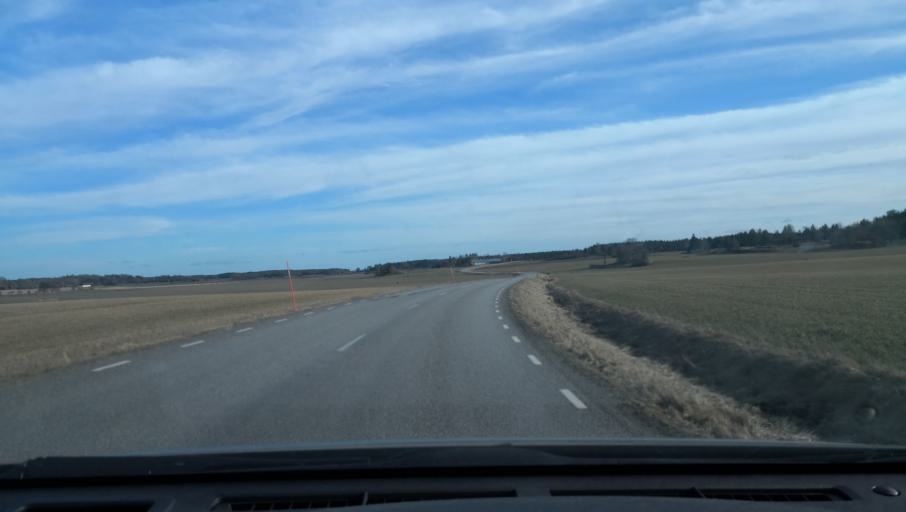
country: SE
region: Uppsala
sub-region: Enkopings Kommun
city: Enkoping
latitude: 59.6141
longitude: 17.1077
